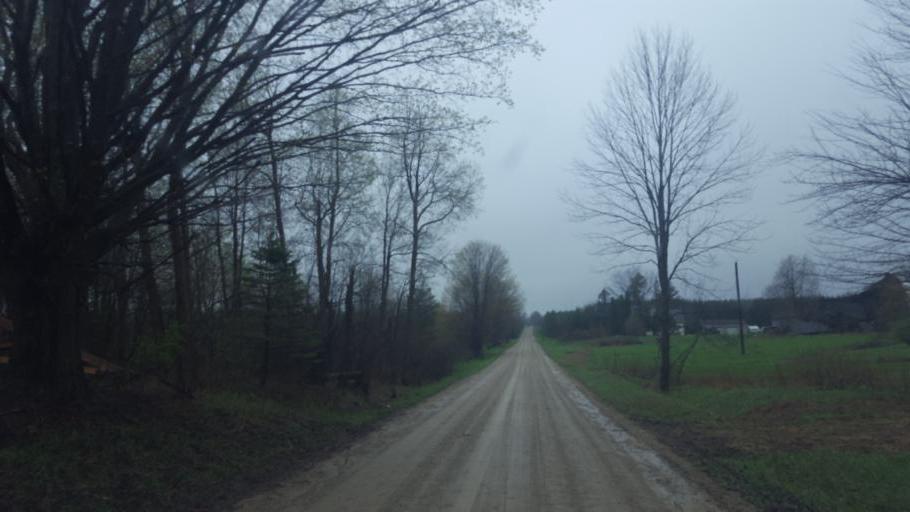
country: US
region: Michigan
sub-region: Isabella County
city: Lake Isabella
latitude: 43.5817
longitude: -85.0162
